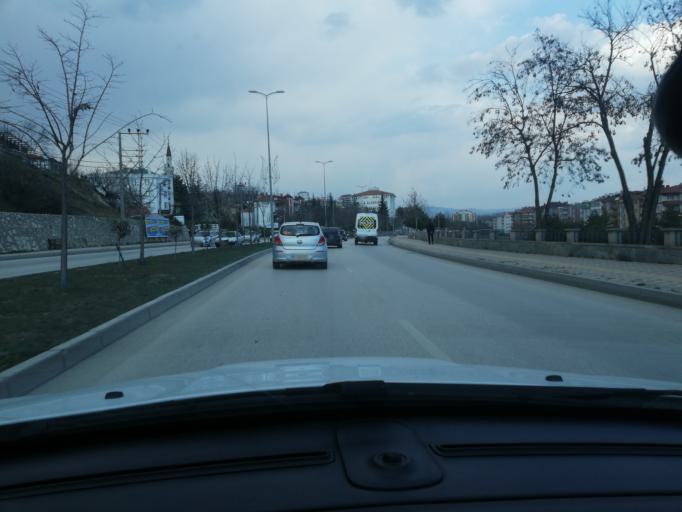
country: TR
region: Kastamonu
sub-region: Cide
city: Kastamonu
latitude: 41.3998
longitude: 33.7809
